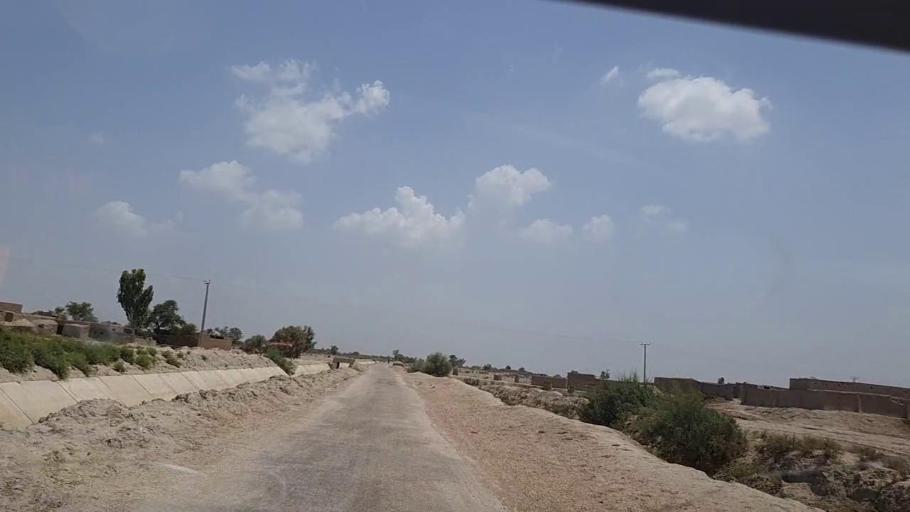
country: PK
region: Sindh
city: Bhan
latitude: 26.5295
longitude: 67.6332
